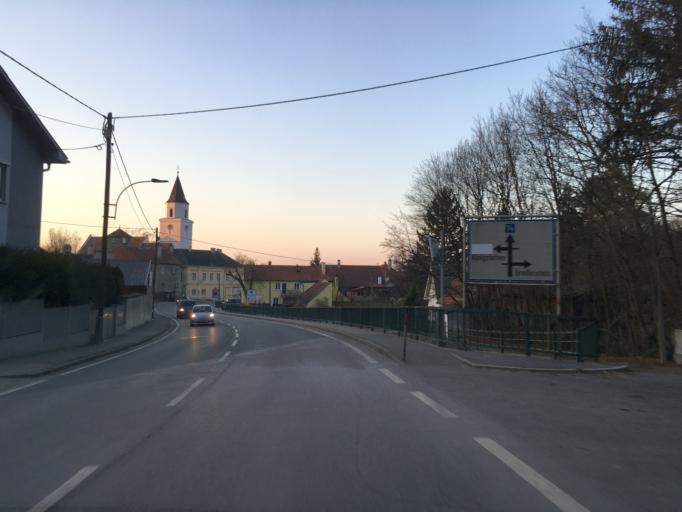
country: AT
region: Lower Austria
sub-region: Politischer Bezirk Tulln
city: Wordern
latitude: 48.3199
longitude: 16.2090
